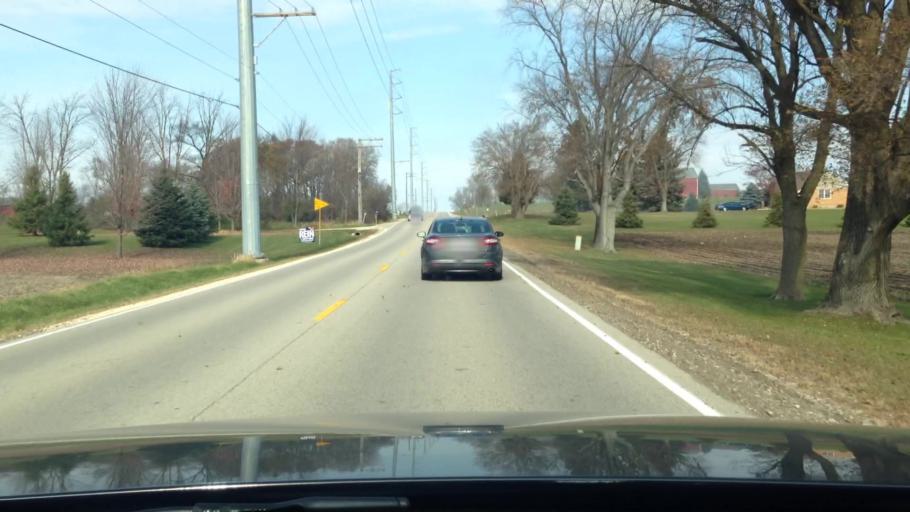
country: US
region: Illinois
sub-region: McHenry County
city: Woodstock
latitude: 42.2865
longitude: -88.4526
